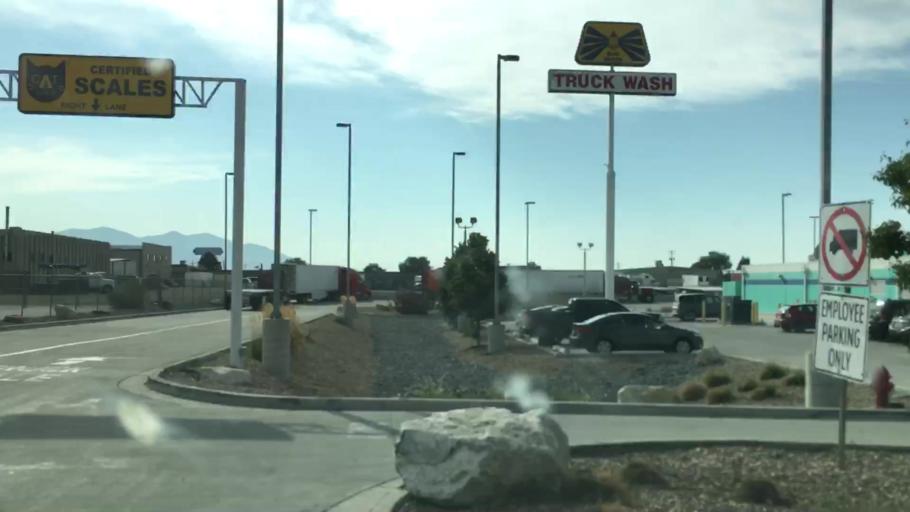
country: US
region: Utah
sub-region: Salt Lake County
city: South Salt Lake
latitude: 40.7268
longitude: -111.9170
